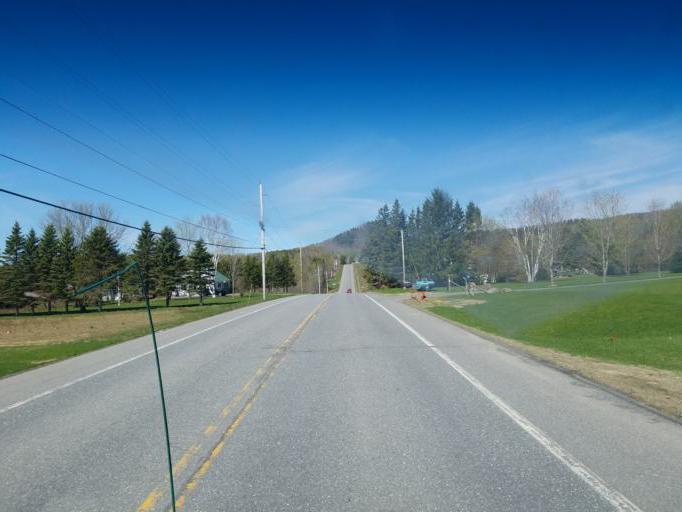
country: US
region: Maine
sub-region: Aroostook County
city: Presque Isle
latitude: 46.6667
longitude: -68.2127
